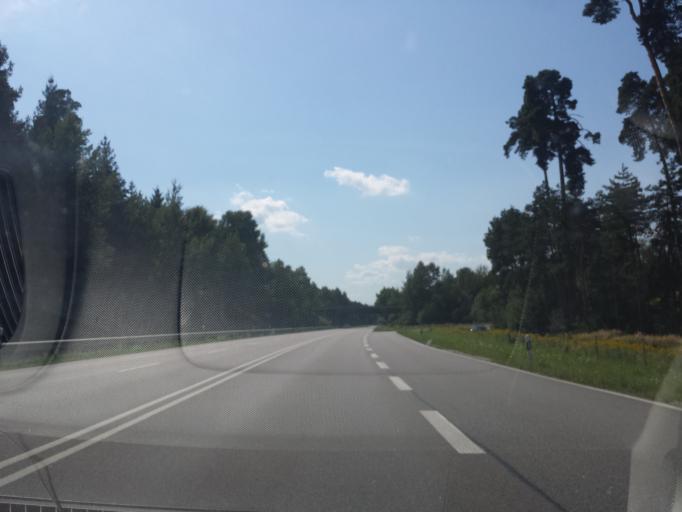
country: DE
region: Bavaria
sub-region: Upper Bavaria
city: Munchsmunster
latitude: 48.7586
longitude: 11.7189
